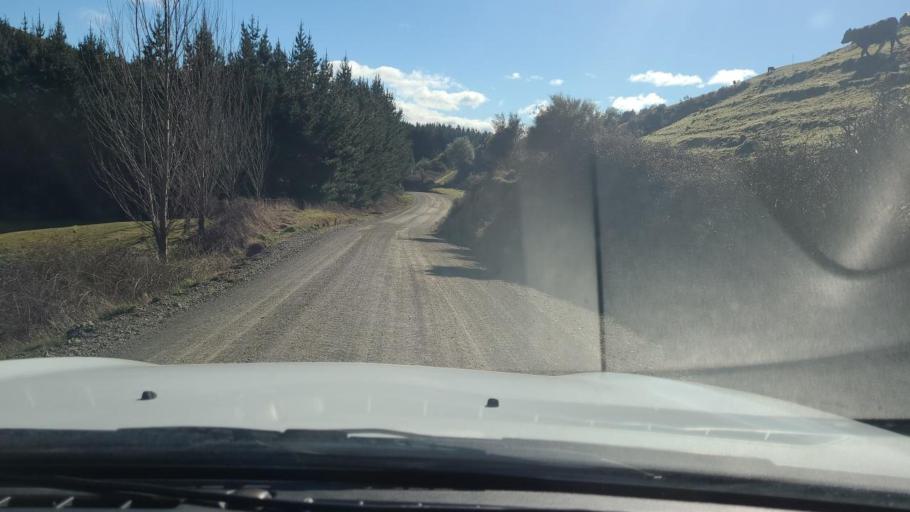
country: NZ
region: Hawke's Bay
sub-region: Napier City
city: Taradale
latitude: -39.2170
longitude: 176.5071
